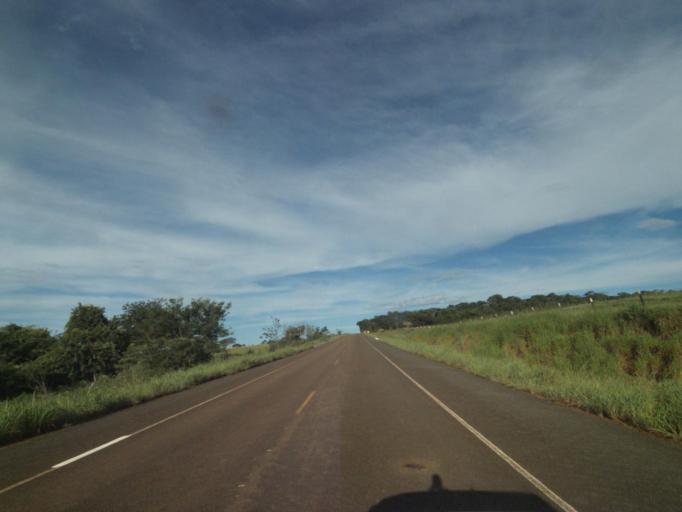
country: BR
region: Goias
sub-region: Jaragua
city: Jaragua
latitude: -15.8924
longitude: -49.4892
